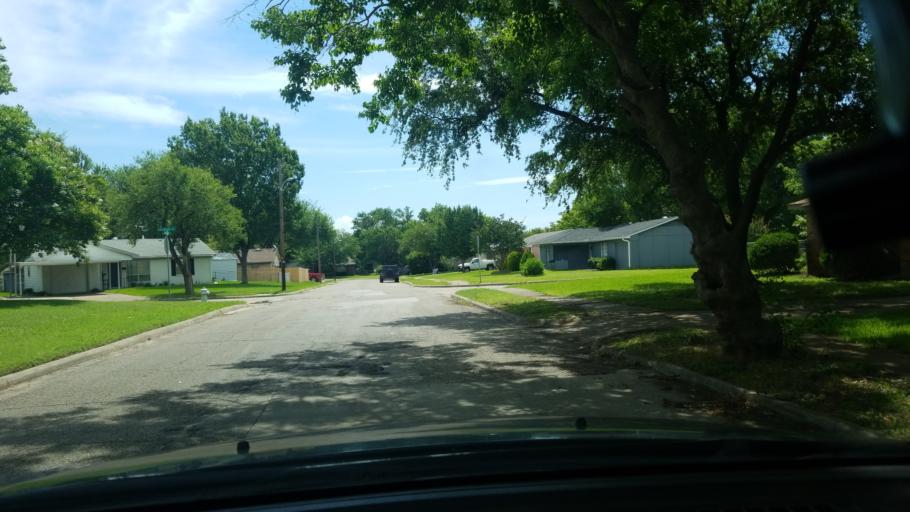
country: US
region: Texas
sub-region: Dallas County
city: Mesquite
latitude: 32.7535
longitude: -96.5803
